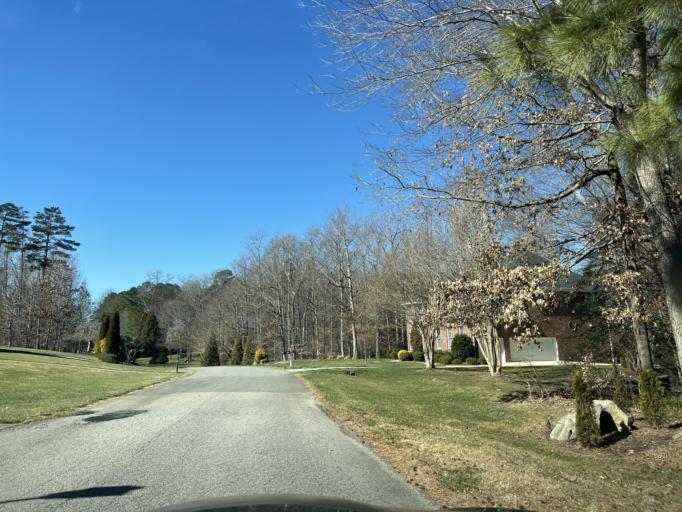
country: US
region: North Carolina
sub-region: Wake County
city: West Raleigh
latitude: 35.9015
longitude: -78.6180
